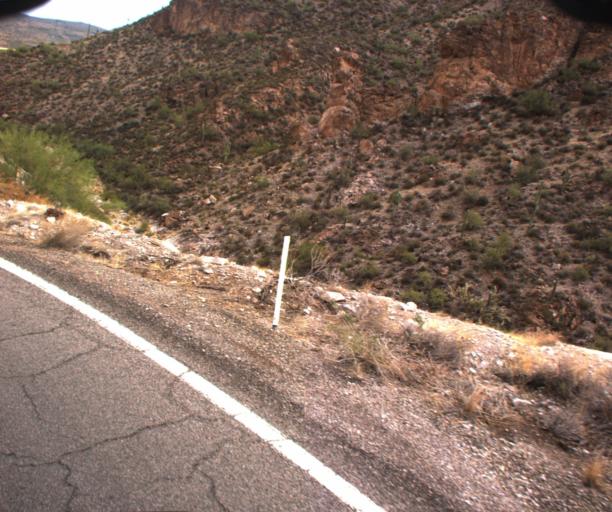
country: US
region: Arizona
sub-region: Pinal County
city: Apache Junction
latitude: 33.5312
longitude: -111.3804
